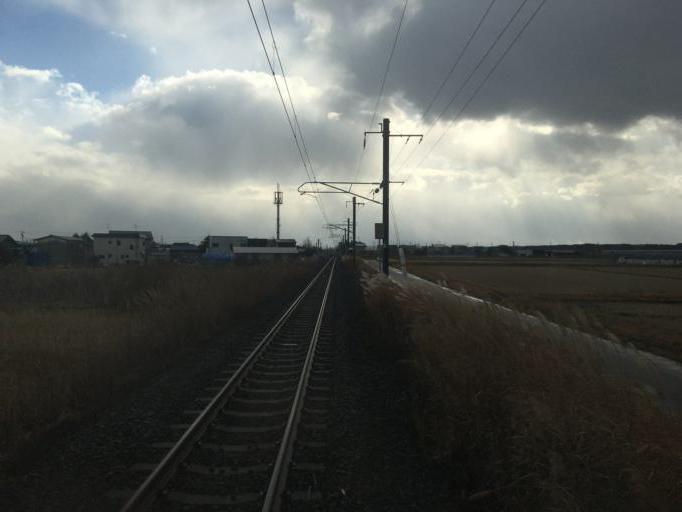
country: JP
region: Aomori
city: Aomori Shi
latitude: 40.8838
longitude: 140.6754
